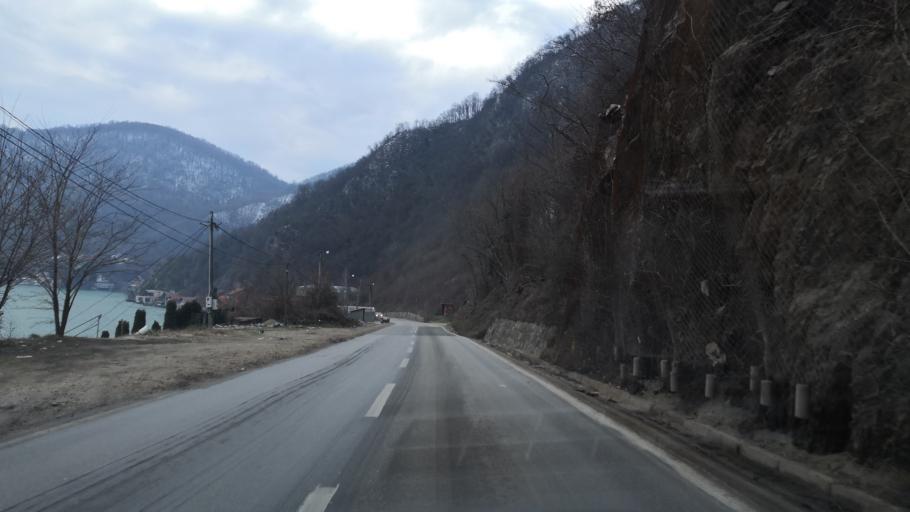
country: RS
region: Central Serbia
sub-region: Macvanski Okrug
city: Mali Zvornik
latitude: 44.3609
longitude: 19.1093
